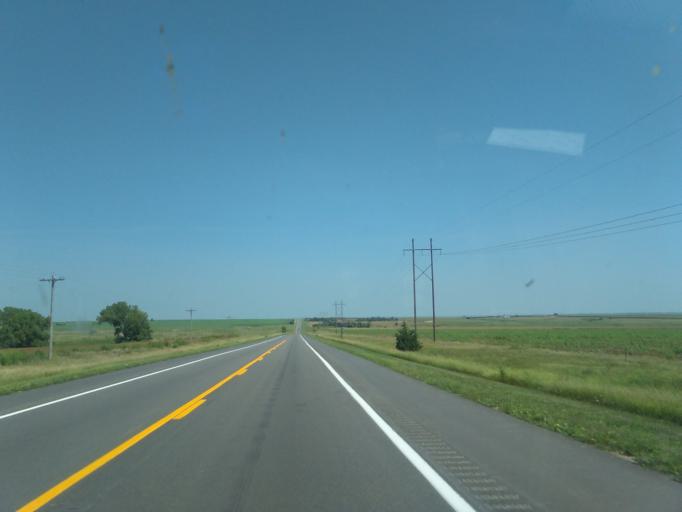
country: US
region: Nebraska
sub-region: Red Willow County
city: McCook
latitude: 40.2826
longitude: -100.6498
